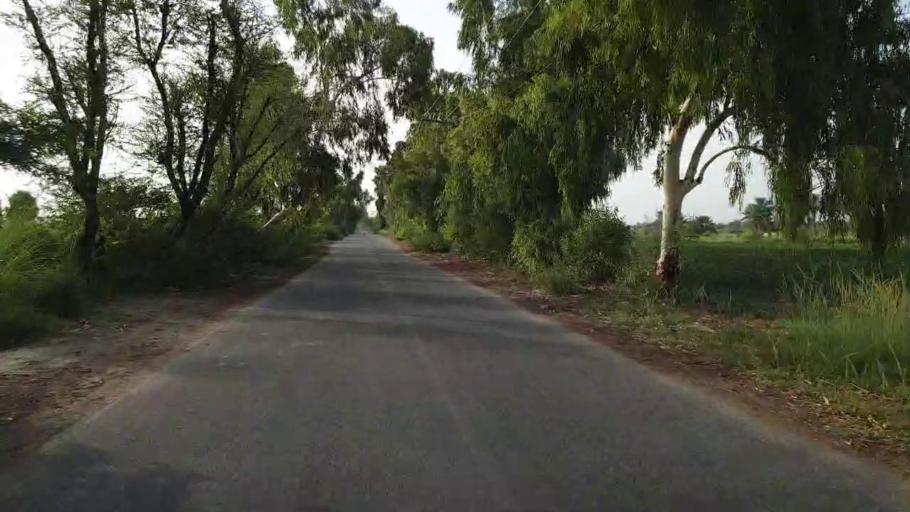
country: PK
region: Sindh
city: Bozdar
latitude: 27.1080
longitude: 68.9607
